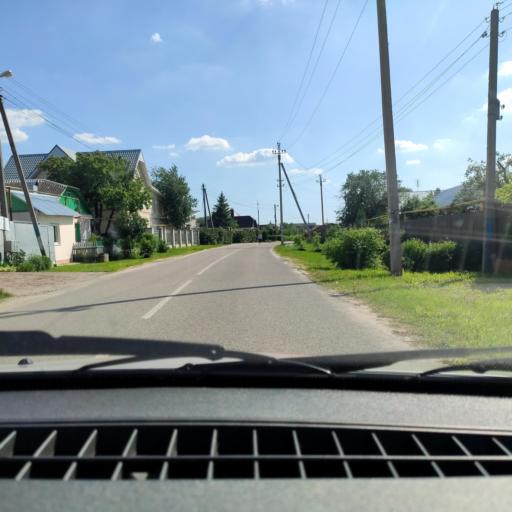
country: RU
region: Voronezj
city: Ramon'
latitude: 51.8146
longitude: 39.2637
